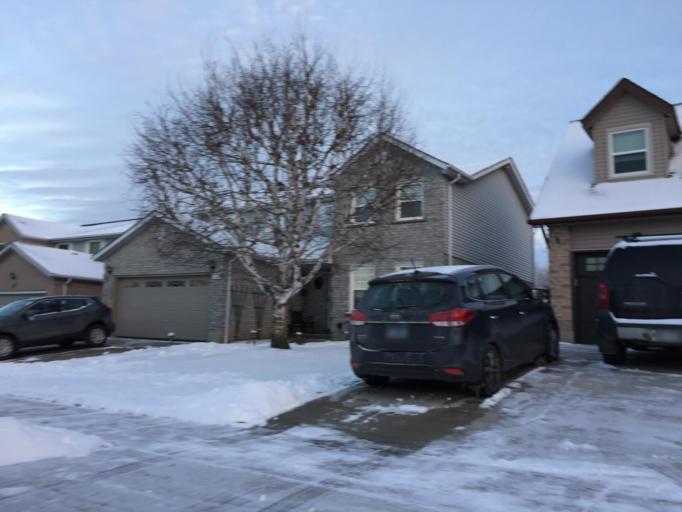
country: CA
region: Ontario
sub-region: Wellington County
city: Guelph
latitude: 43.5194
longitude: -80.2851
